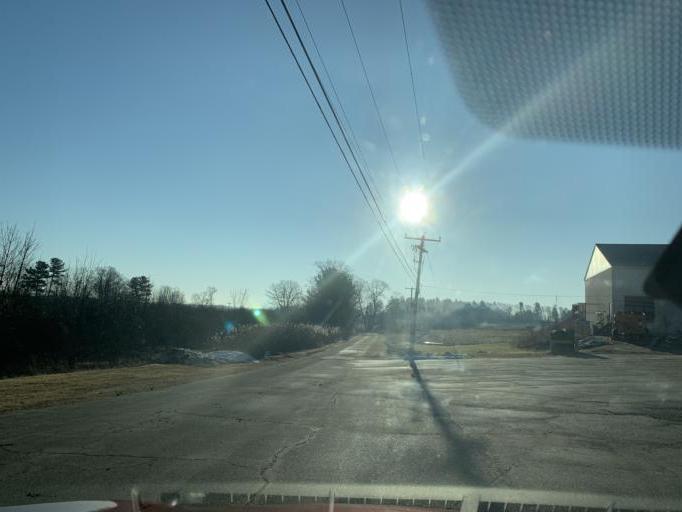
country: US
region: New Hampshire
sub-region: Rockingham County
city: Derry
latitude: 42.8776
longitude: -71.3501
